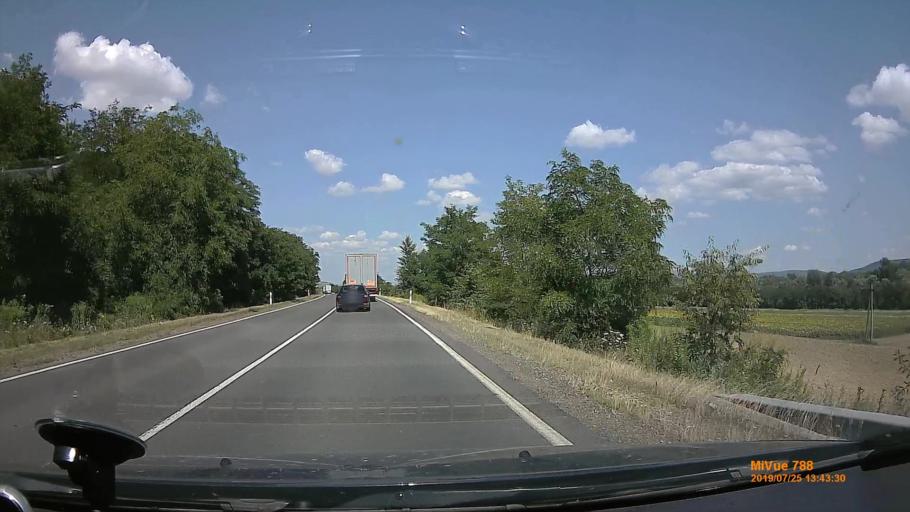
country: HU
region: Borsod-Abauj-Zemplen
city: Gonc
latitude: 48.4578
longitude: 21.1942
